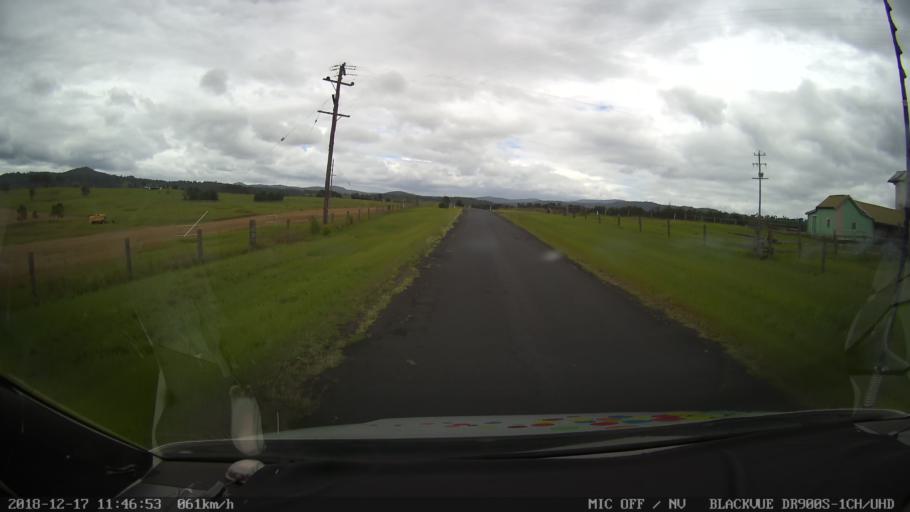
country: AU
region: New South Wales
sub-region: Kyogle
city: Kyogle
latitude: -28.6327
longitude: 152.5924
